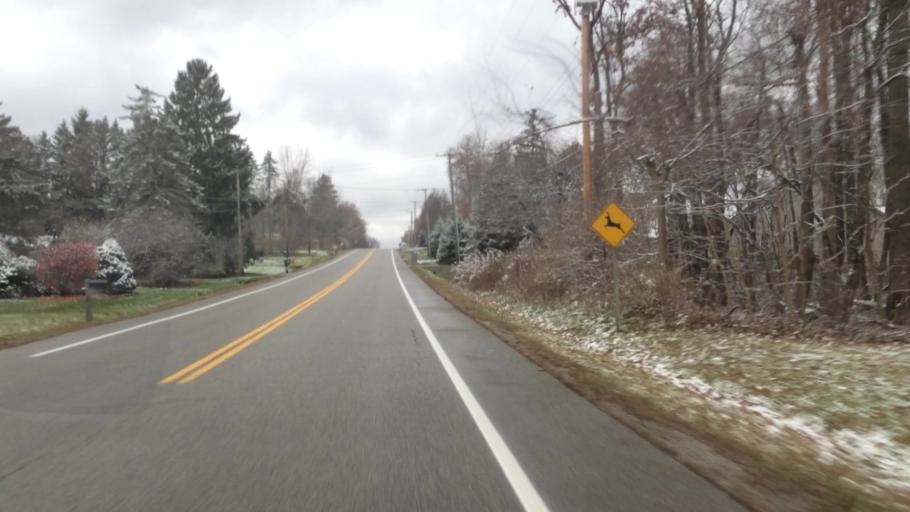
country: US
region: Ohio
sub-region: Summit County
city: Macedonia
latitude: 41.3046
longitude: -81.5313
